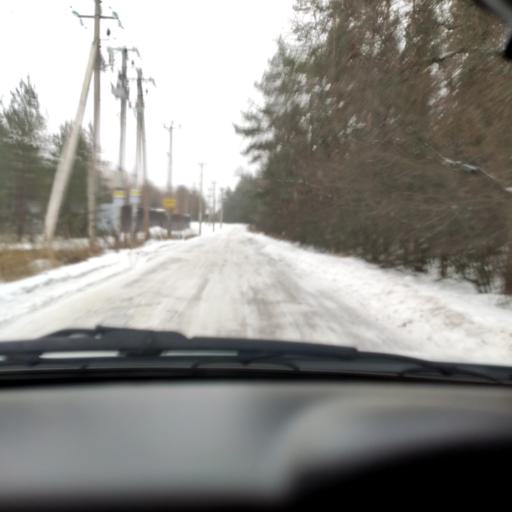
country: RU
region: Voronezj
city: Ramon'
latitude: 51.8866
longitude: 39.2541
